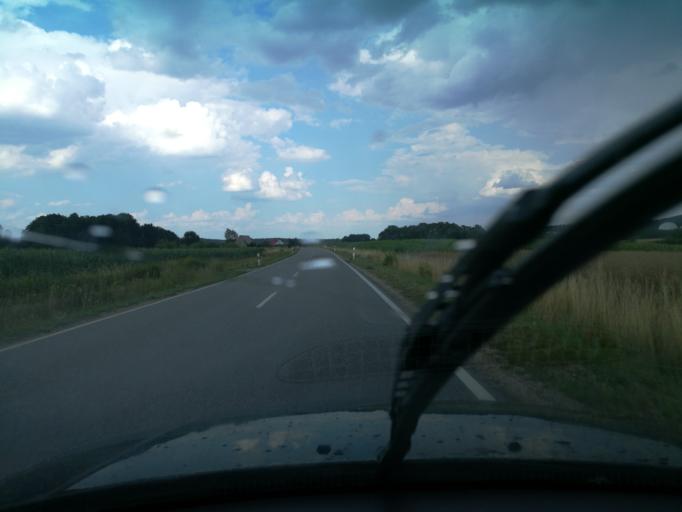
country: DE
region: Bavaria
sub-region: Regierungsbezirk Mittelfranken
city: Langenzenn
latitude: 49.4625
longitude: 10.7664
